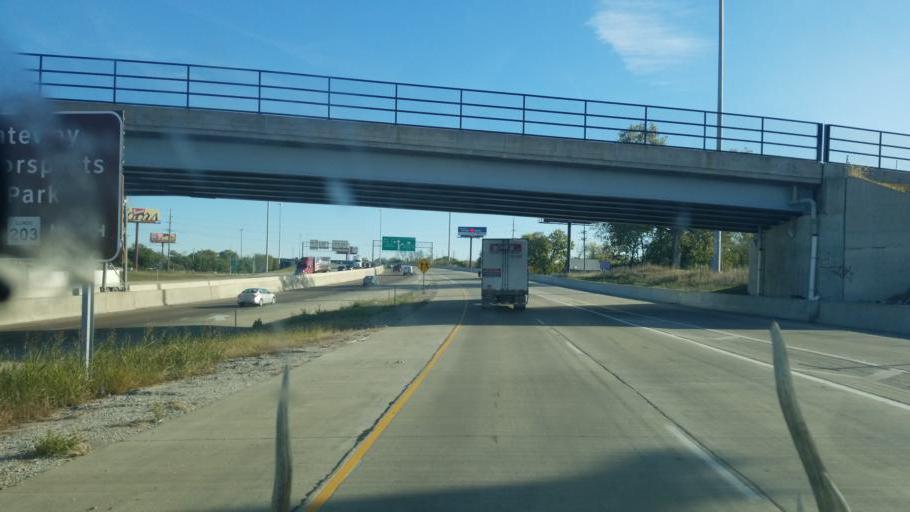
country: US
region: Illinois
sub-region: Saint Clair County
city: East Saint Louis
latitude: 38.6338
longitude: -90.1406
